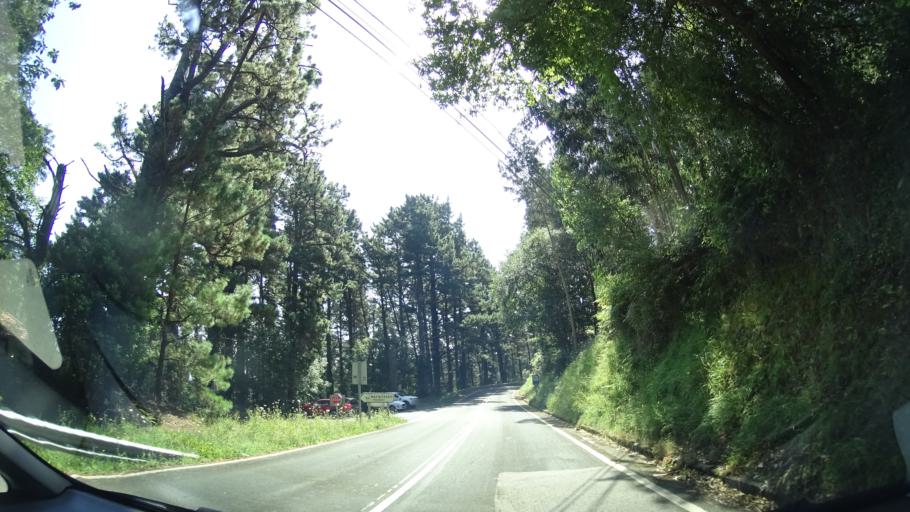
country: ES
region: Basque Country
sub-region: Bizkaia
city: Bermeo
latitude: 43.4349
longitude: -2.7471
